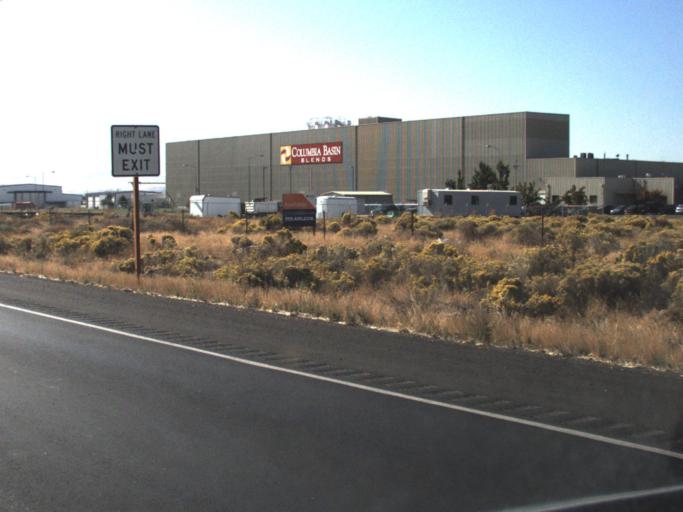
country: US
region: Washington
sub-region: Franklin County
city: Pasco
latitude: 46.2621
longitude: -119.0860
